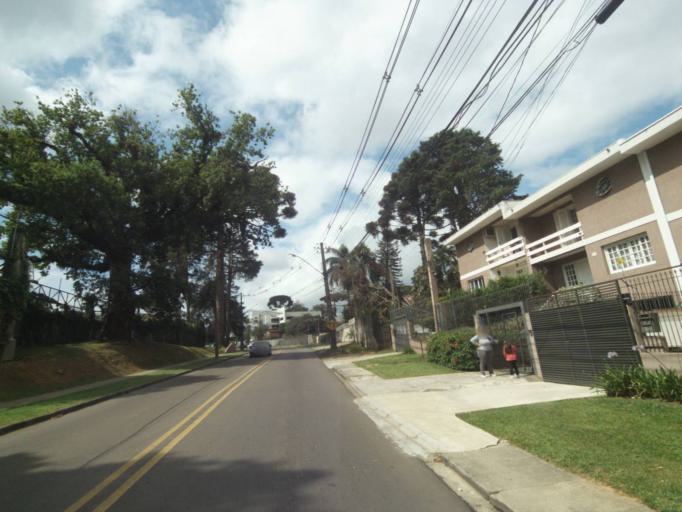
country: BR
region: Parana
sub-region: Curitiba
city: Curitiba
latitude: -25.3846
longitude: -49.2820
